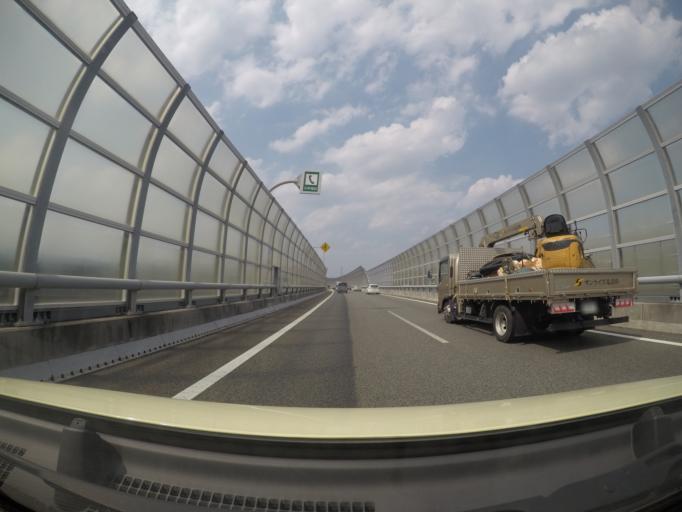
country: JP
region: Tokyo
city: Fussa
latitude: 35.7189
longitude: 139.2839
